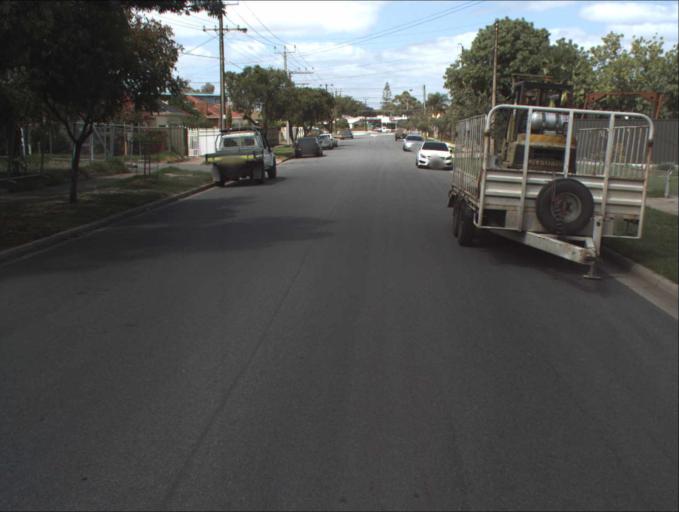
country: AU
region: South Australia
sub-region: Charles Sturt
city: Woodville
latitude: -34.8790
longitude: 138.5575
